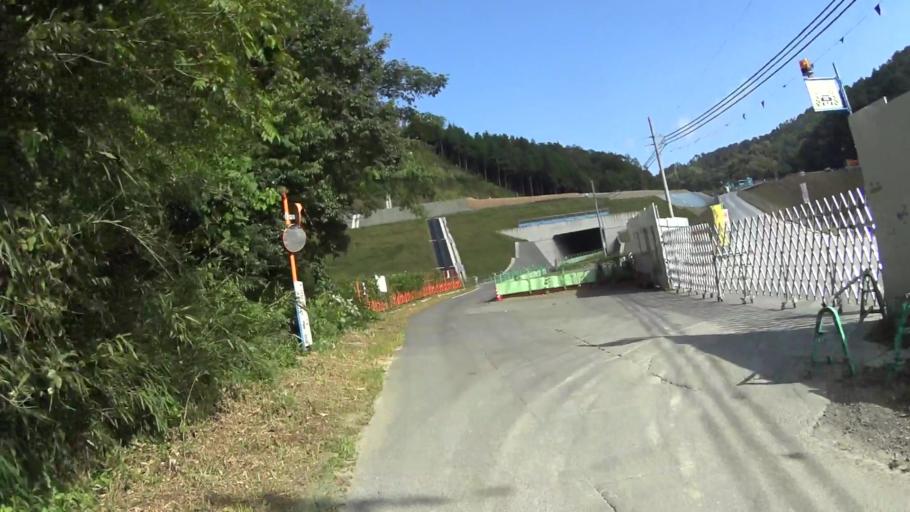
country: JP
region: Kyoto
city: Miyazu
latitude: 35.5675
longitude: 135.1194
